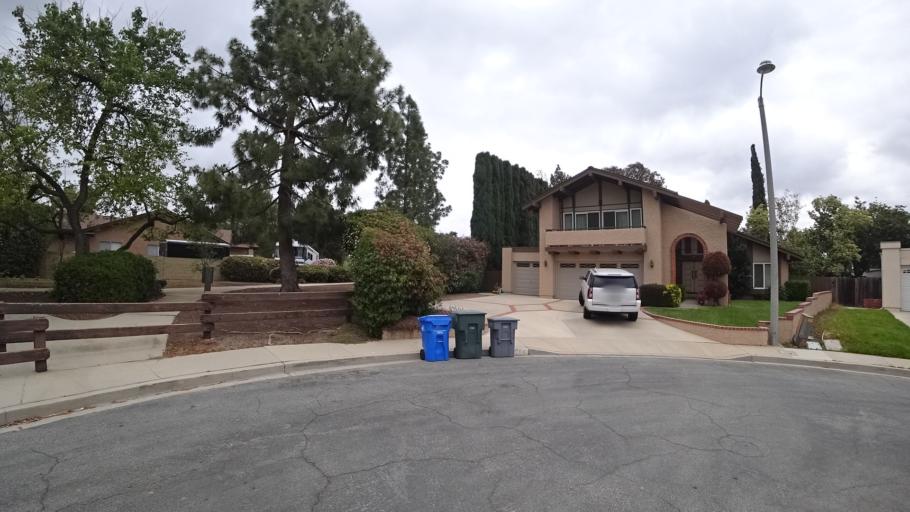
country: US
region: California
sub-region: Ventura County
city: Casa Conejo
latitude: 34.2213
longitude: -118.8984
